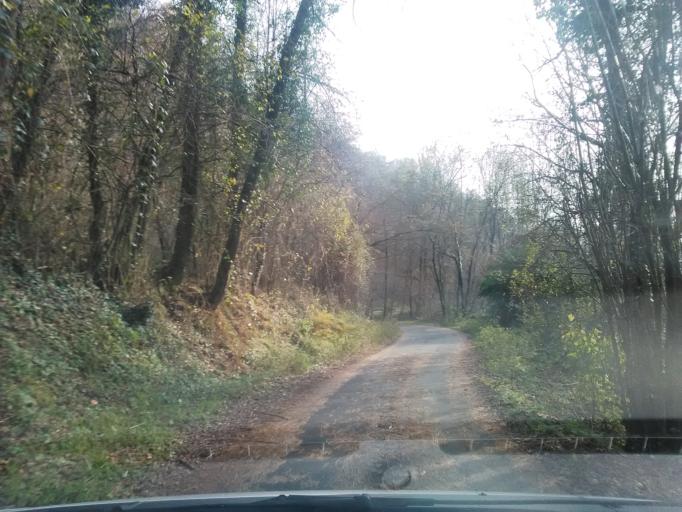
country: IT
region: Piedmont
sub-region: Provincia di Vercelli
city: Postua
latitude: 45.7063
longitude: 8.2355
